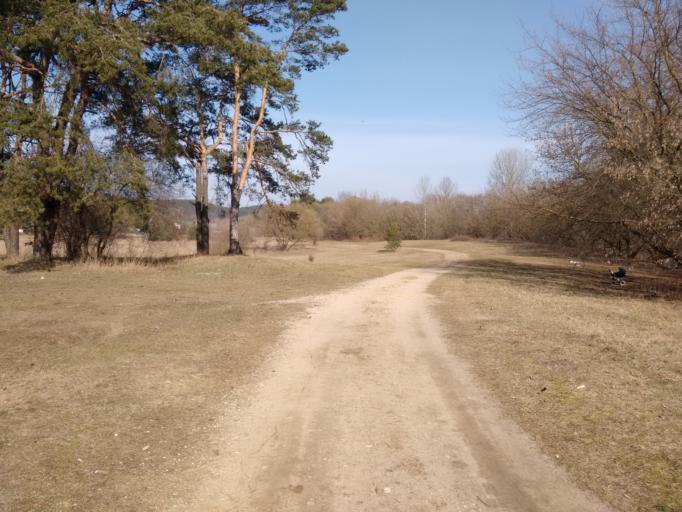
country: LT
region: Vilnius County
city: Vilkpede
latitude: 54.6766
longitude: 25.2305
